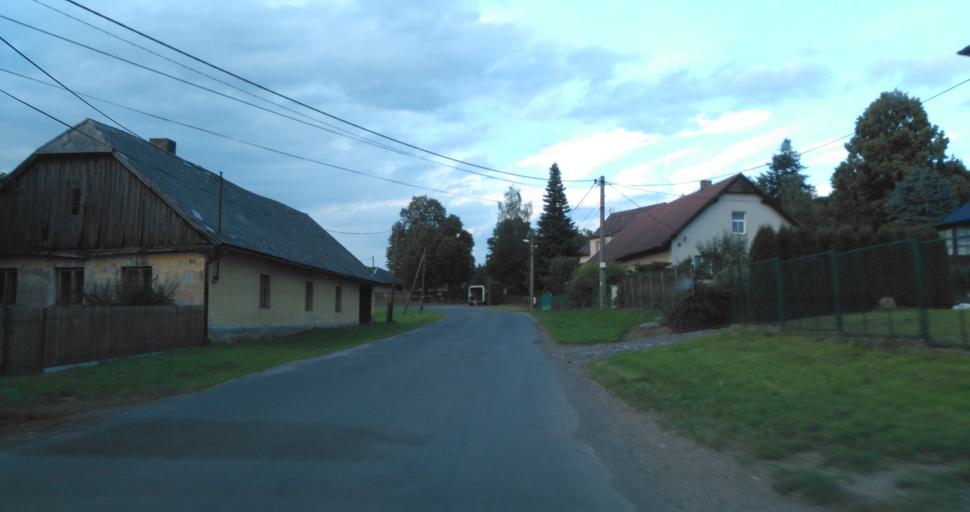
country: CZ
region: Plzensky
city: Zbiroh
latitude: 49.8427
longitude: 13.7404
